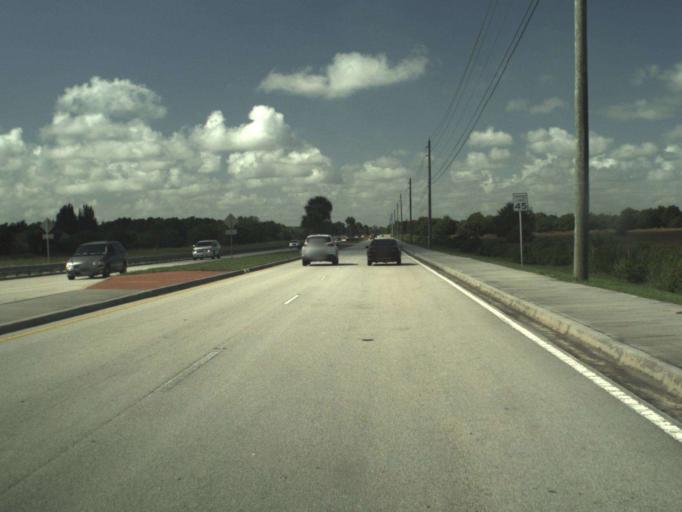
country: US
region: Florida
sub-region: Indian River County
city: Vero Beach South
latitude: 27.5941
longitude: -80.4474
